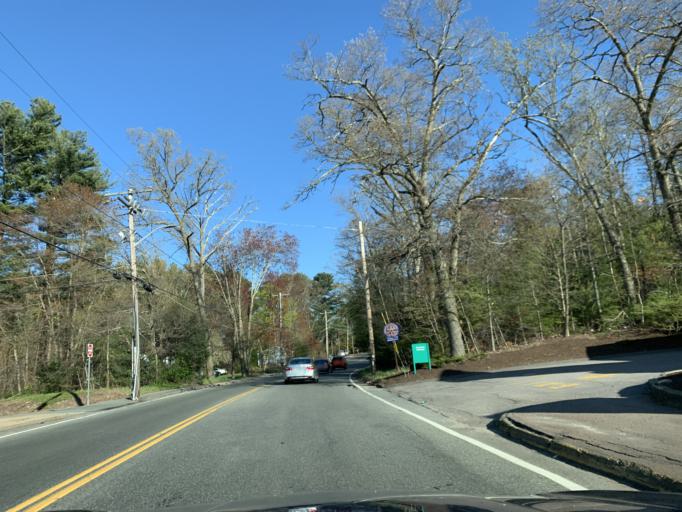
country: US
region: Massachusetts
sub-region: Norfolk County
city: Canton
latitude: 42.1375
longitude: -71.1473
